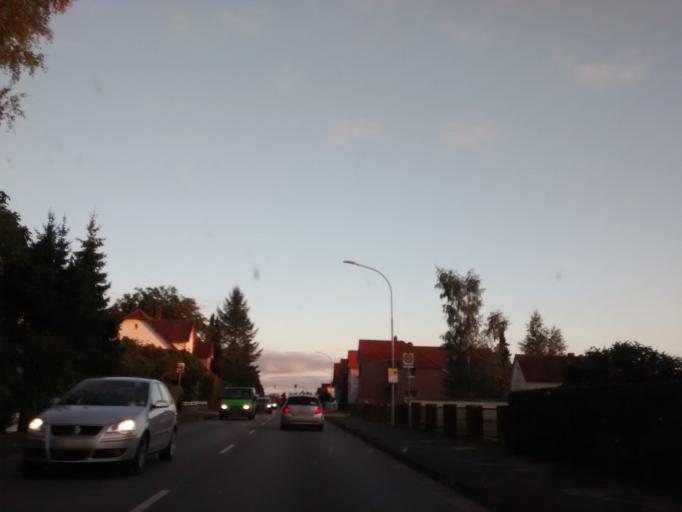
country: DE
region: North Rhine-Westphalia
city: Halle
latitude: 52.0571
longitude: 8.3686
